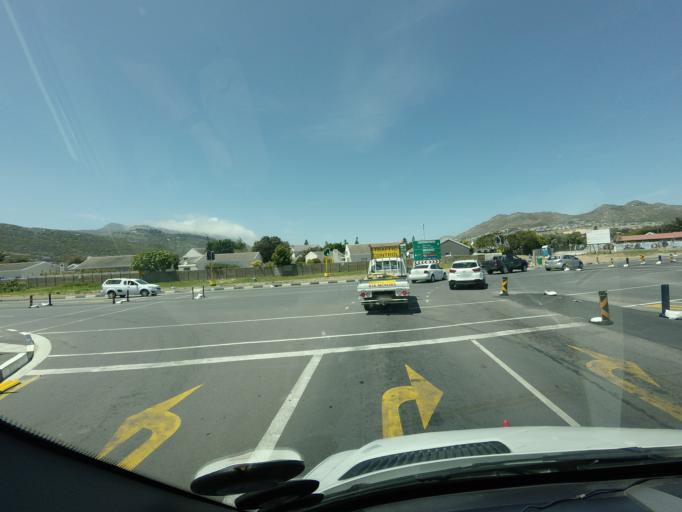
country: ZA
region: Western Cape
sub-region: City of Cape Town
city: Constantia
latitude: -34.1210
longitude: 18.3915
